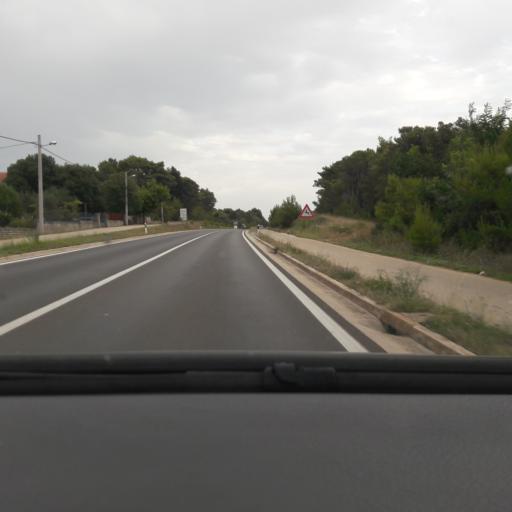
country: HR
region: Zadarska
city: Zadar
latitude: 44.1677
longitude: 15.1992
